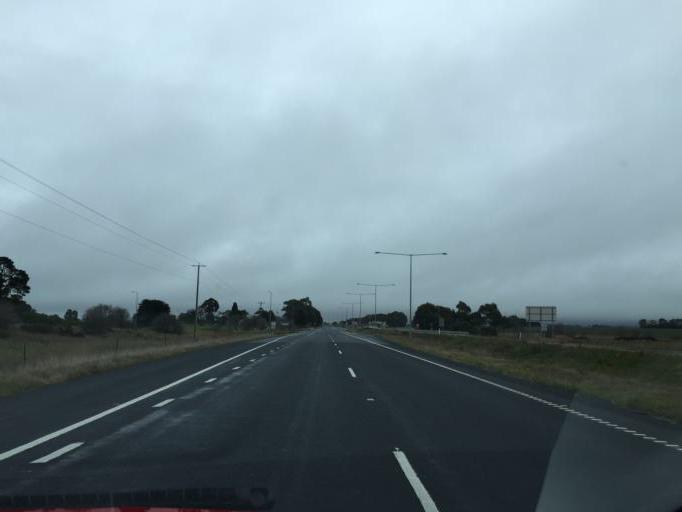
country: AU
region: Victoria
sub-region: Ballarat North
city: Newington
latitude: -37.4799
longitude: 143.7143
